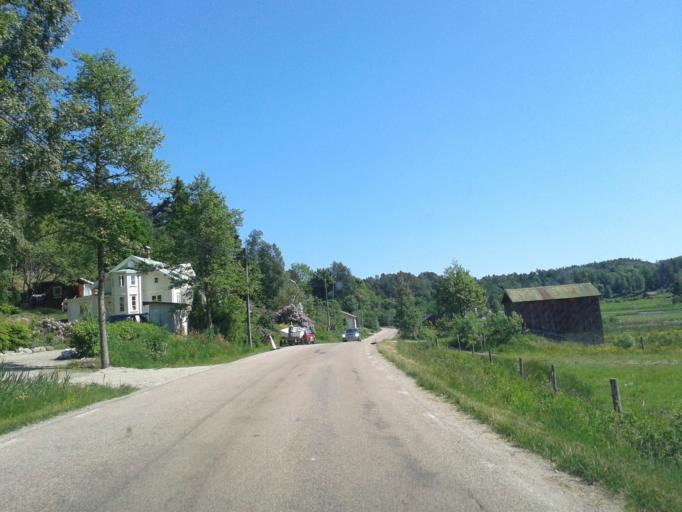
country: SE
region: Vaestra Goetaland
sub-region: Orust
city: Henan
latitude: 58.2565
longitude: 11.7540
